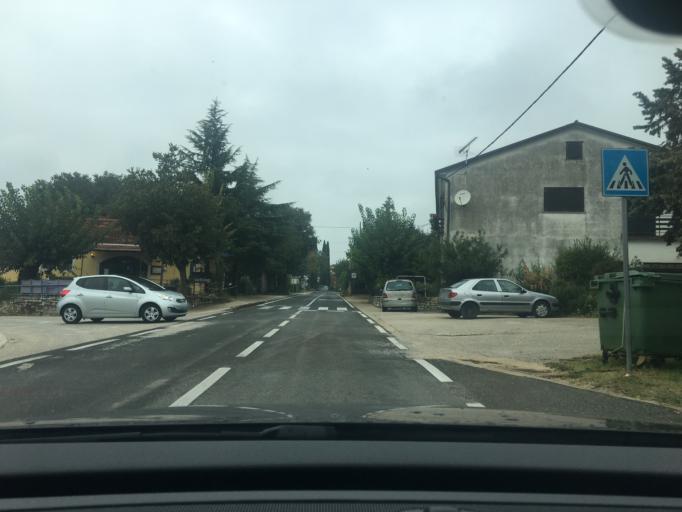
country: HR
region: Istarska
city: Buje
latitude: 45.4423
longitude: 13.6566
